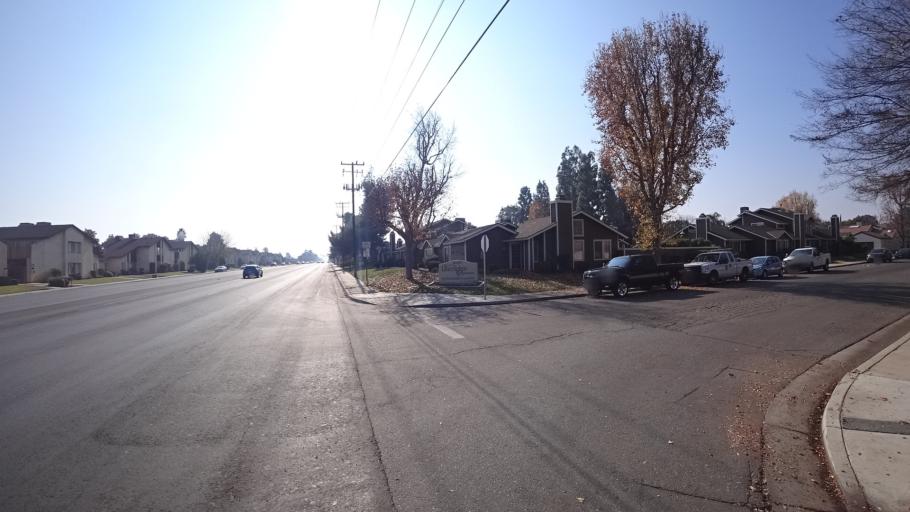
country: US
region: California
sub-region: Kern County
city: Greenacres
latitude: 35.3329
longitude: -119.0746
